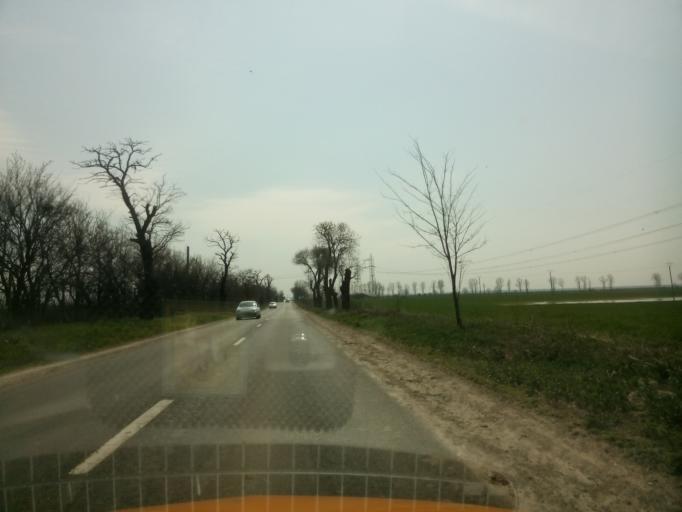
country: RO
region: Giurgiu
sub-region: Comuna Herasti
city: Herasti
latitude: 44.2551
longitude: 26.3640
